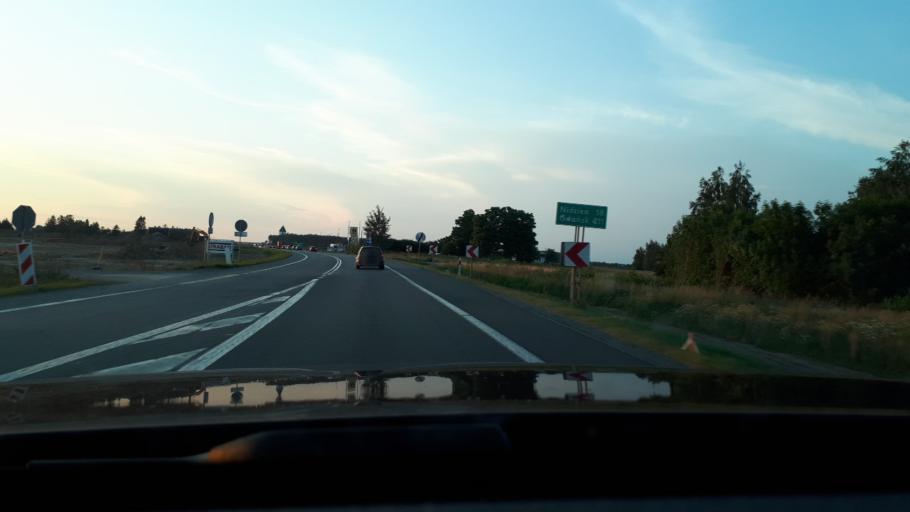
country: PL
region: Masovian Voivodeship
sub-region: Powiat mlawski
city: Wieczfnia Koscielna
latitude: 53.1980
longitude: 20.4363
